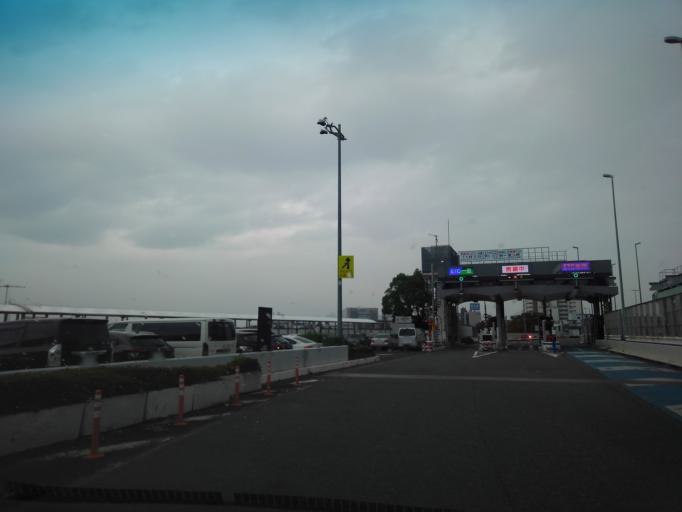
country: JP
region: Tokyo
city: Tokyo
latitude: 35.6681
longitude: 139.6436
